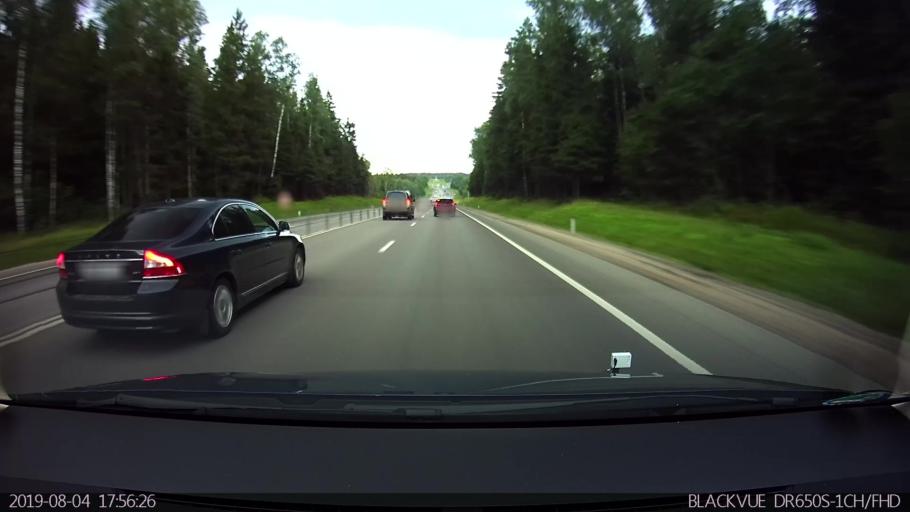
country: RU
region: Moskovskaya
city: Uvarovka
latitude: 55.4642
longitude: 35.7451
